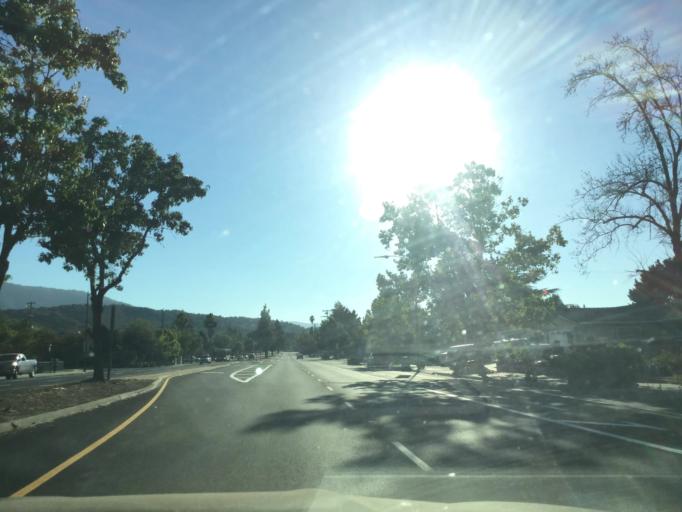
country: US
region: California
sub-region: Santa Clara County
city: Cambrian Park
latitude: 37.2222
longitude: -121.8705
